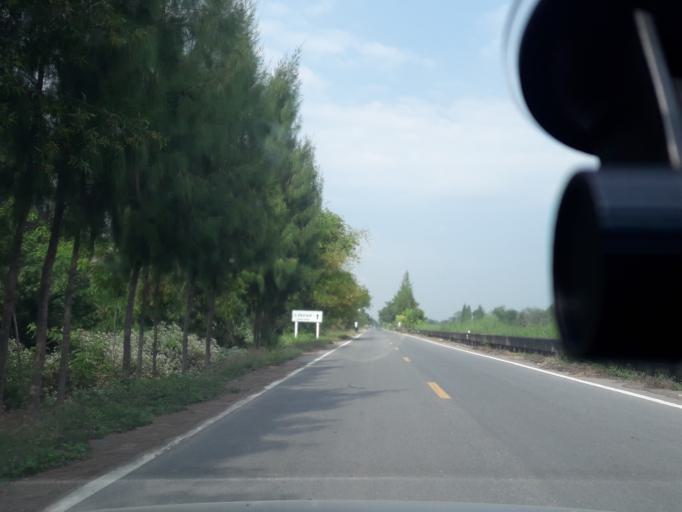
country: TH
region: Pathum Thani
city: Nong Suea
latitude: 14.2159
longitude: 100.8915
